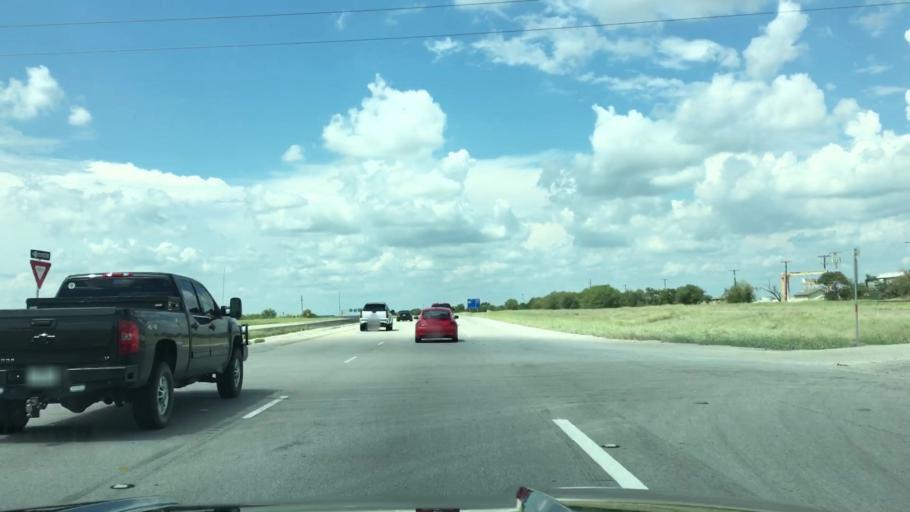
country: US
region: Texas
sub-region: Wise County
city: Rhome
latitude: 33.0358
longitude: -97.4526
